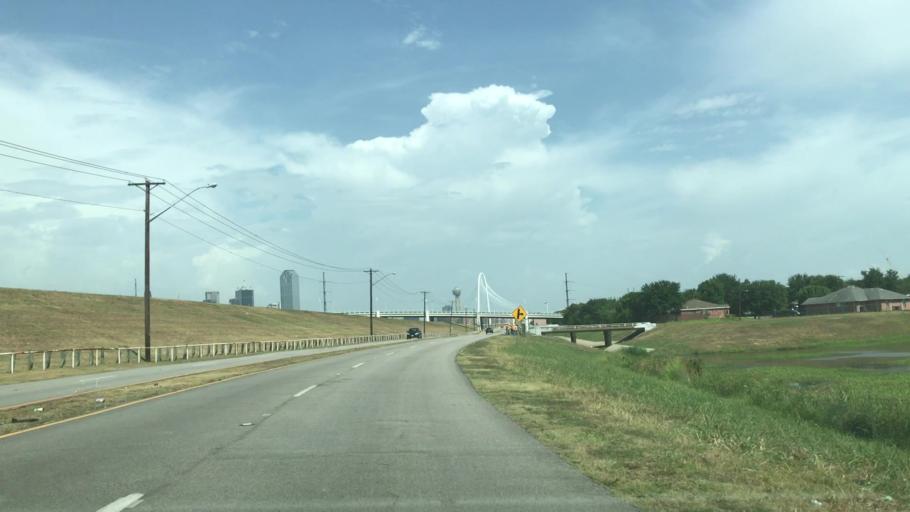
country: US
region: Texas
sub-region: Dallas County
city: Dallas
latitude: 32.7884
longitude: -96.8414
